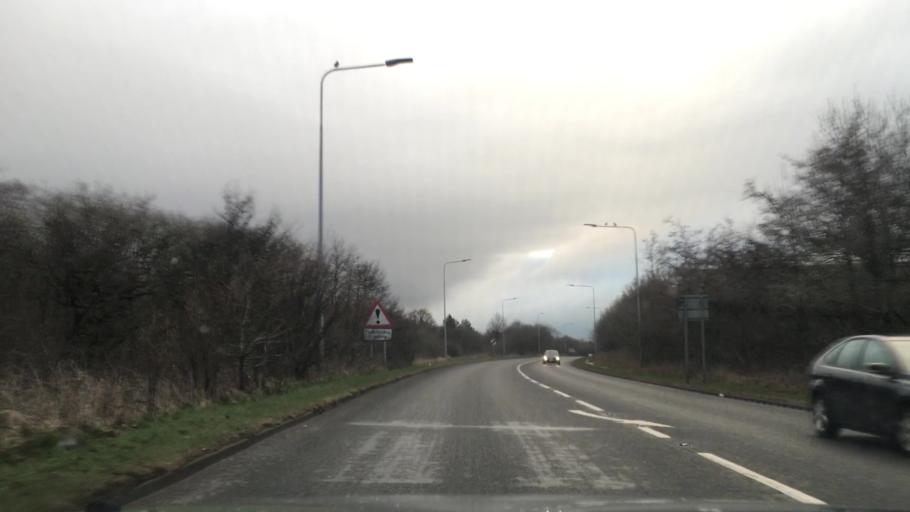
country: GB
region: England
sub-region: Cumbria
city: Askam in Furness
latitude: 54.1485
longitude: -3.2291
